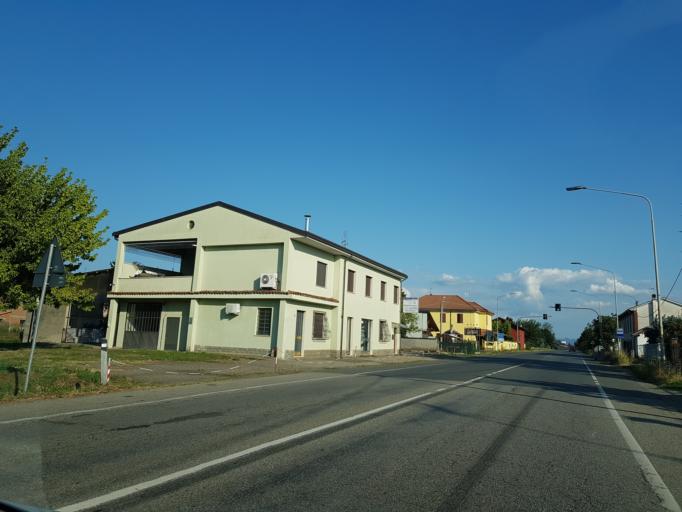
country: IT
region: Piedmont
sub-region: Provincia di Alessandria
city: Litta Parodi-Cascinagrossa
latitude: 44.8673
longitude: 8.7014
